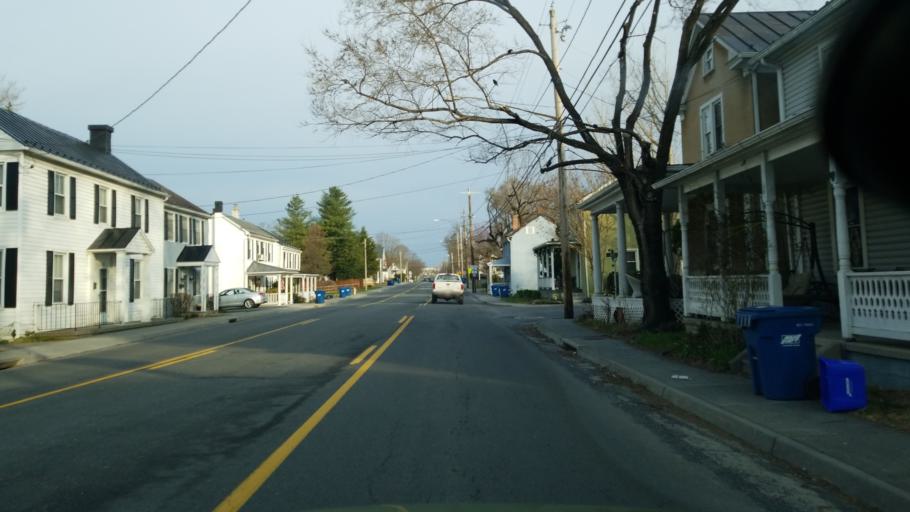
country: US
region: Virginia
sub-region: Clarke County
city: Berryville
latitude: 39.1529
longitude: -77.9845
